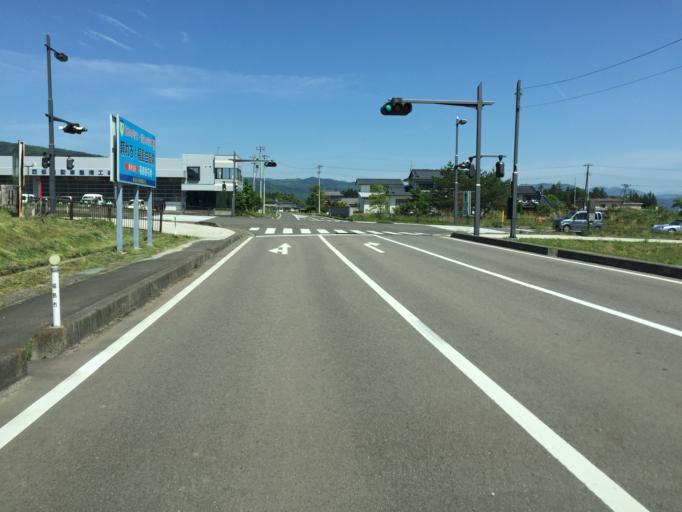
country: JP
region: Fukushima
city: Fukushima-shi
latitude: 37.7217
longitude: 140.3773
